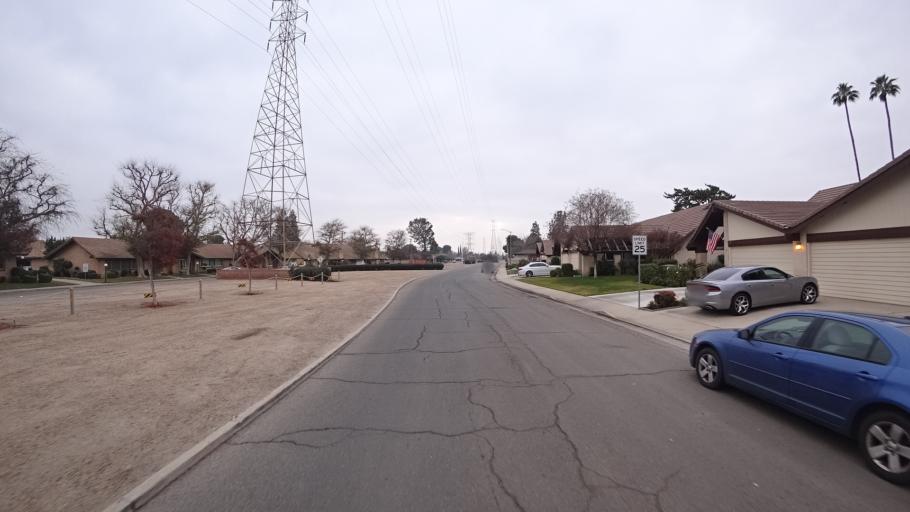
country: US
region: California
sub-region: Kern County
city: Bakersfield
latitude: 35.3920
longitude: -119.0287
